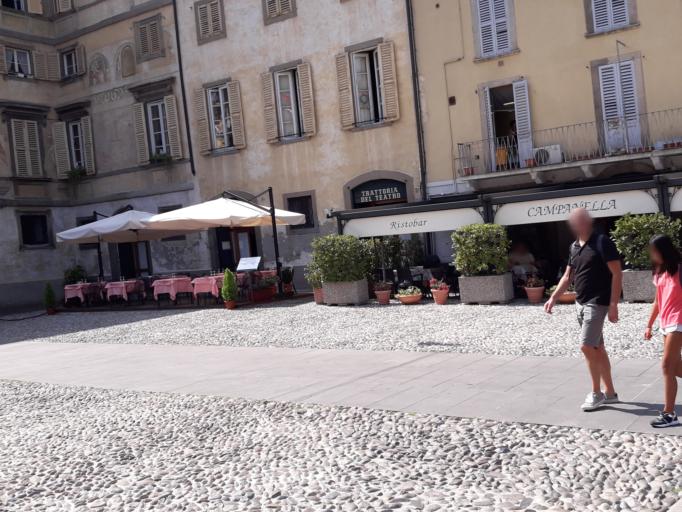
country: IT
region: Lombardy
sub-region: Provincia di Bergamo
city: Bergamo
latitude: 45.7053
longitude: 9.6600
